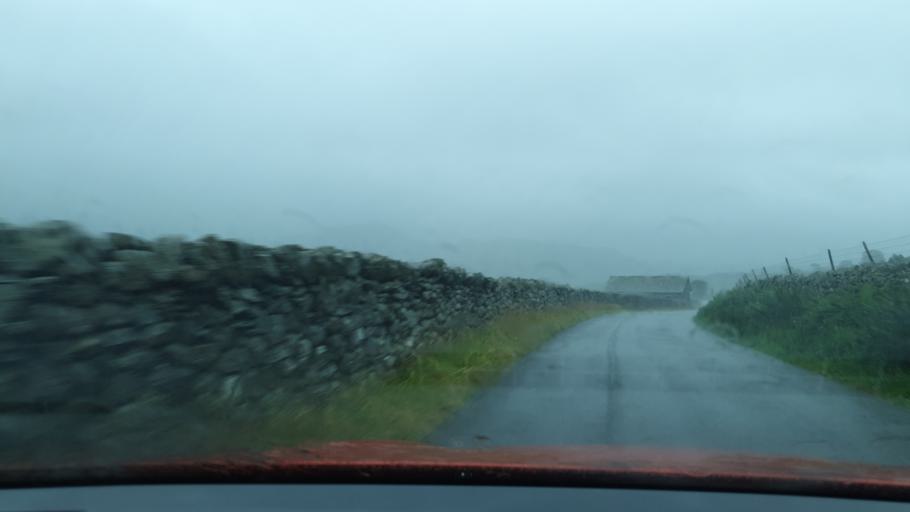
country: GB
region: England
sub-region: Cumbria
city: Millom
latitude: 54.3412
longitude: -3.2460
